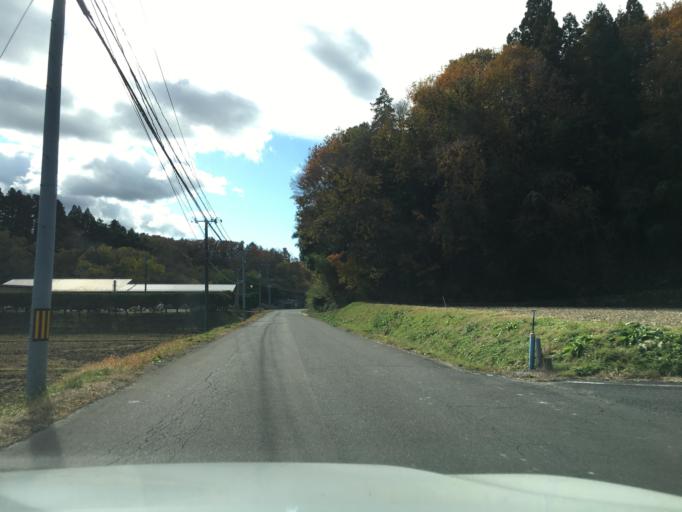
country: JP
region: Fukushima
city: Miharu
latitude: 37.5029
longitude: 140.4883
